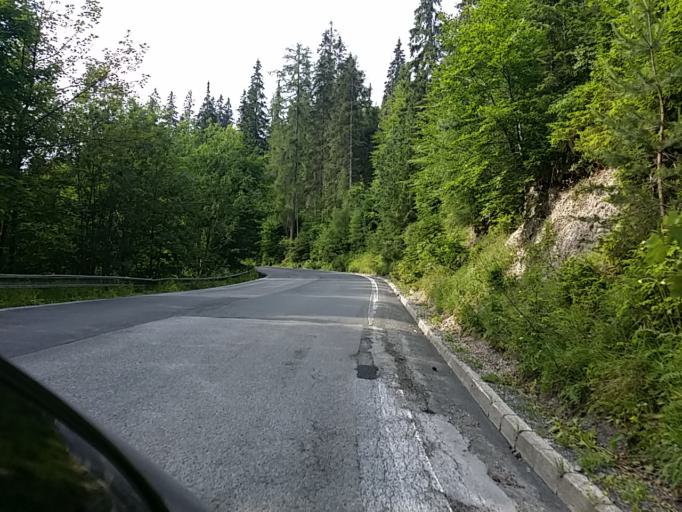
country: SK
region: Kosicky
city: Dobsina
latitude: 48.8979
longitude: 20.2451
